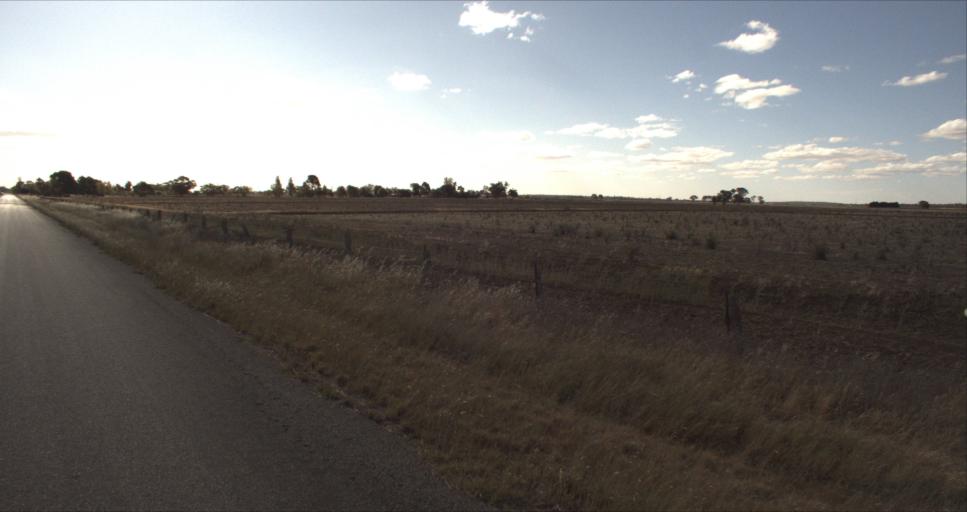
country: AU
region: New South Wales
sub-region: Leeton
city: Leeton
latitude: -34.4395
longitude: 146.2177
